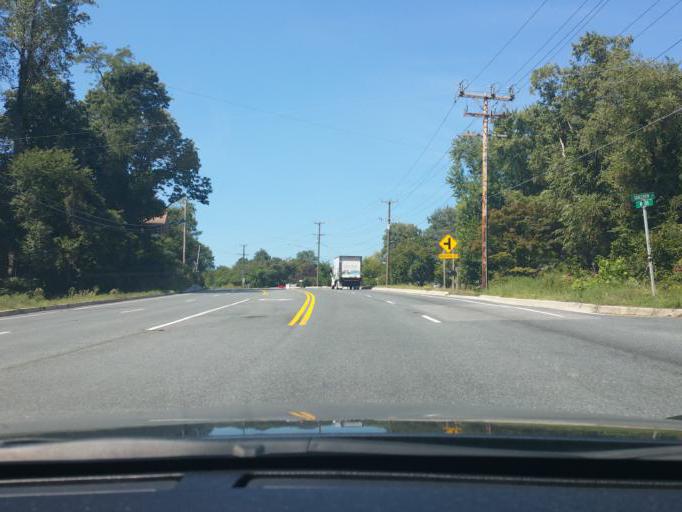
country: US
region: Maryland
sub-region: Harford County
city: Havre de Grace
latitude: 39.5613
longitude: -76.1077
